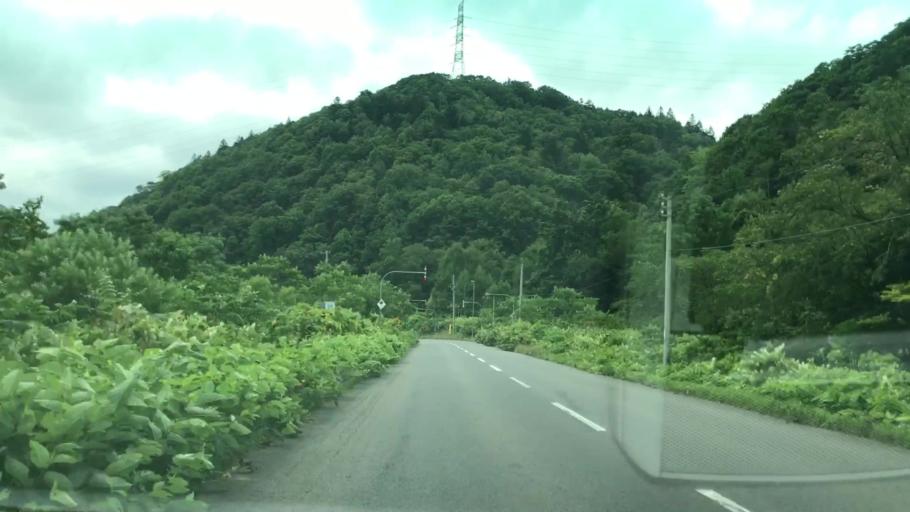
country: JP
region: Hokkaido
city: Yoichi
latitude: 43.0404
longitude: 140.8598
